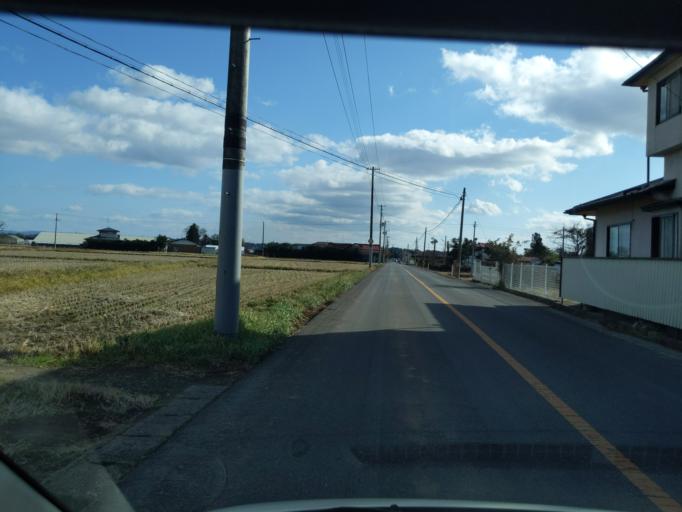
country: JP
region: Miyagi
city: Kogota
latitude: 38.7181
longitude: 141.0774
